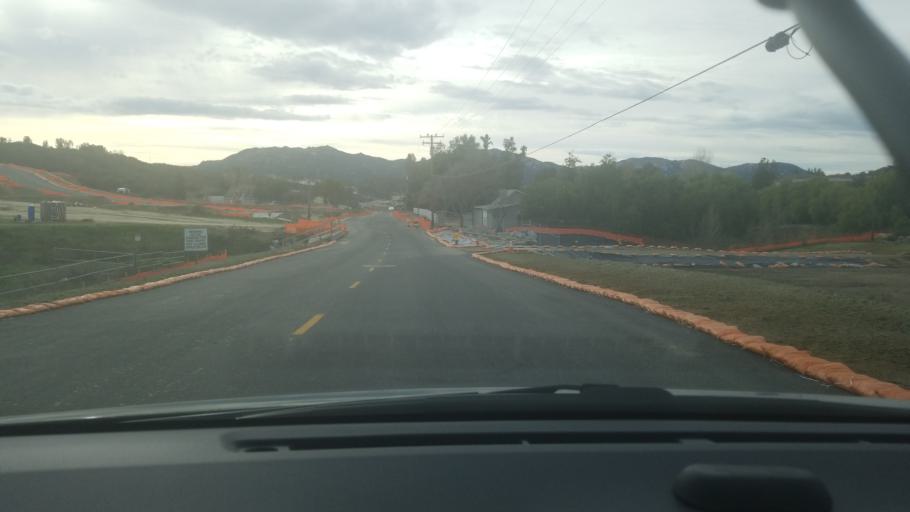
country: US
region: California
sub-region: Riverside County
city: Temecula
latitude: 33.4661
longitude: -117.0705
